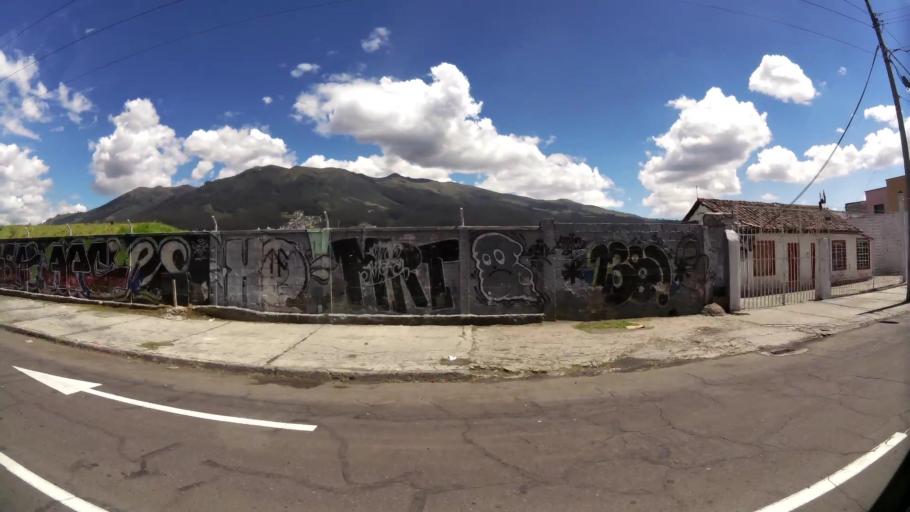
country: EC
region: Pichincha
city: Quito
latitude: -0.1555
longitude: -78.4850
